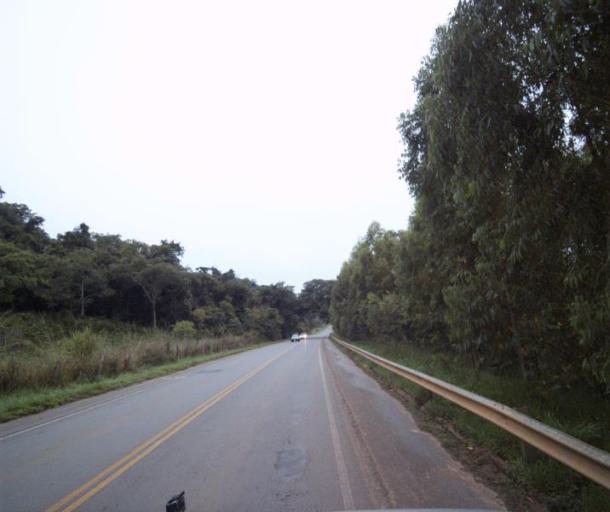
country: BR
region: Goias
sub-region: Pirenopolis
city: Pirenopolis
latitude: -15.9613
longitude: -48.8176
